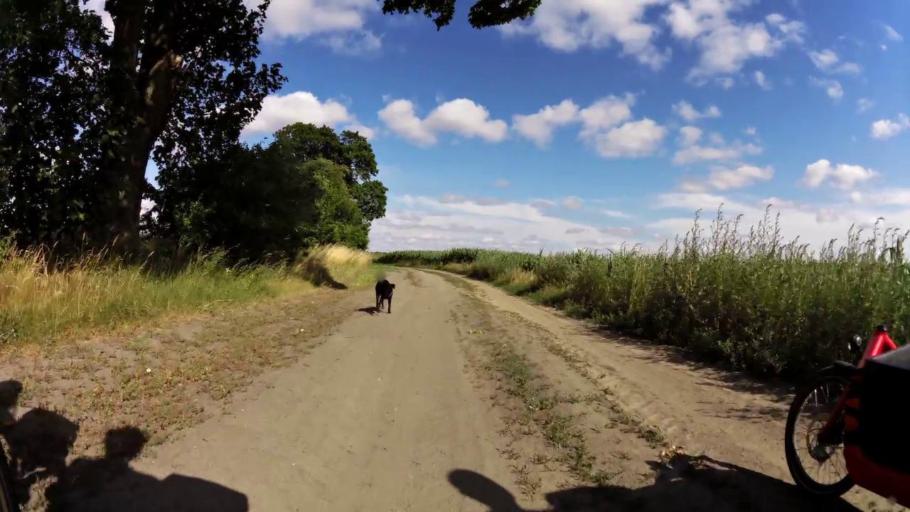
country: PL
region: West Pomeranian Voivodeship
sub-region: Powiat lobeski
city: Lobez
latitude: 53.6721
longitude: 15.6945
